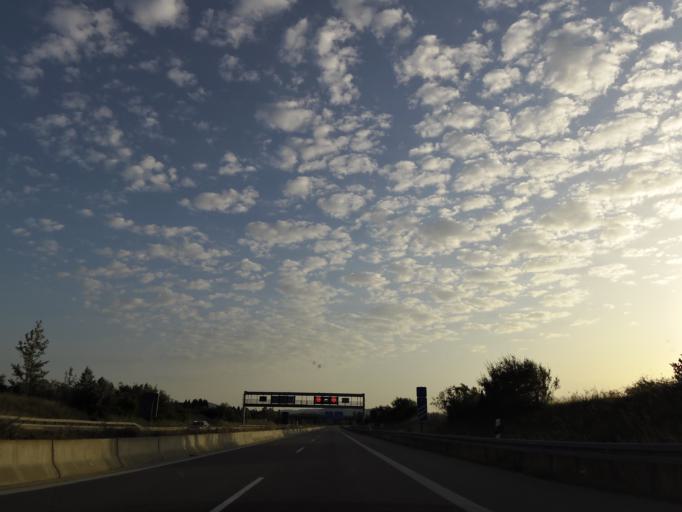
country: AT
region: Tyrol
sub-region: Politischer Bezirk Reutte
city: Vils
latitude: 47.5703
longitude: 10.6600
